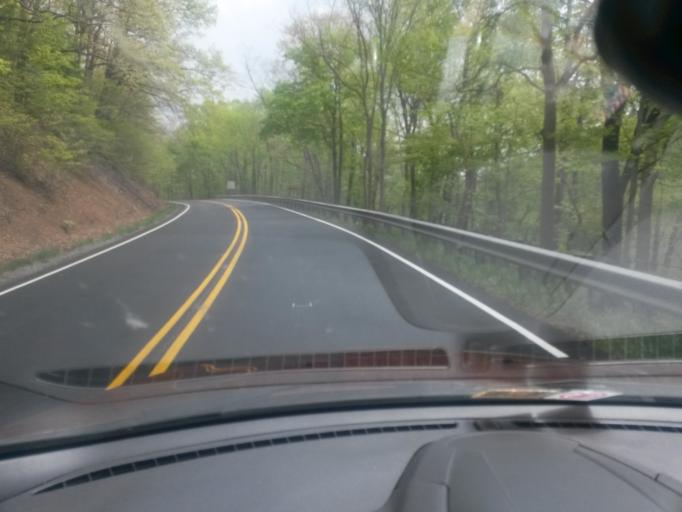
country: US
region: Virginia
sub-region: City of Covington
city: Covington
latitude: 37.8018
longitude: -80.0536
